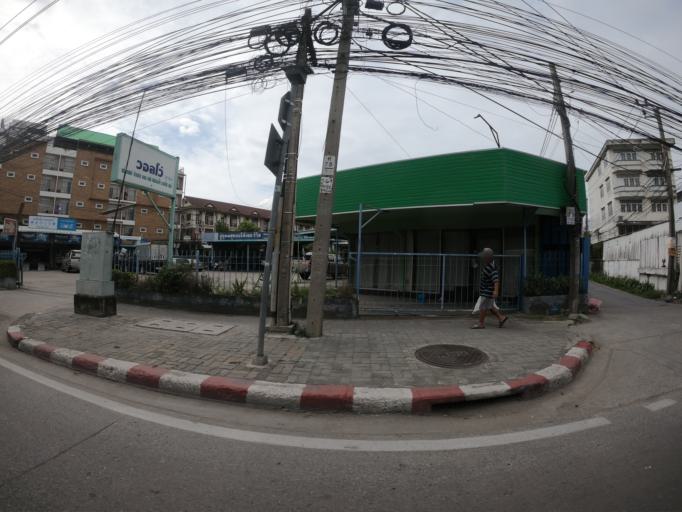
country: TH
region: Bangkok
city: Bang Na
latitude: 13.6769
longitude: 100.6579
